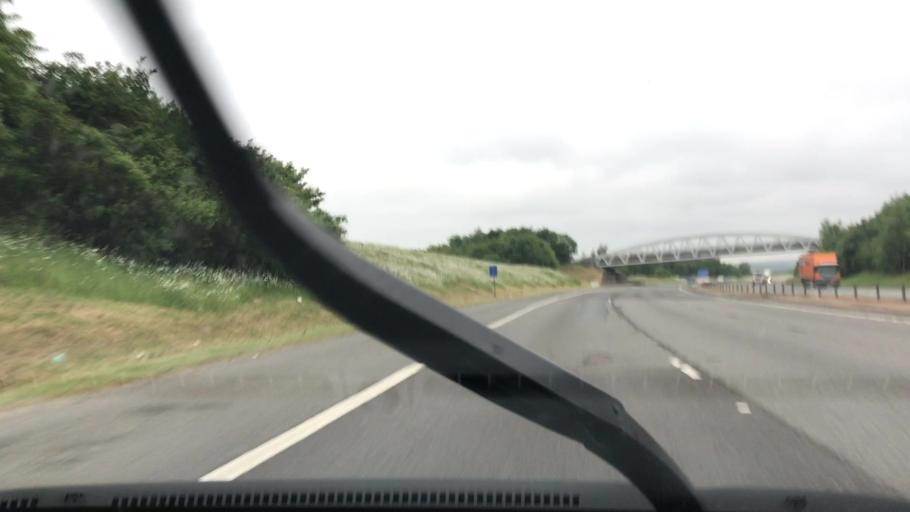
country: GB
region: England
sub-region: City and Borough of Leeds
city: Swillington
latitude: 53.7746
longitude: -1.4371
